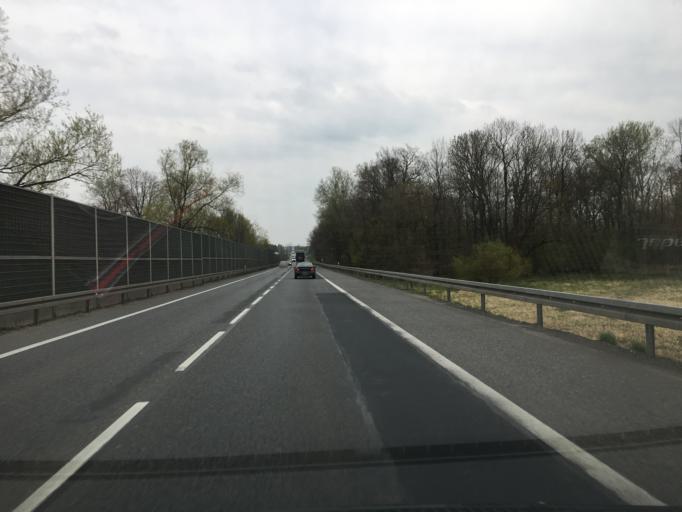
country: PL
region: Lower Silesian Voivodeship
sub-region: Powiat sredzki
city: Sroda Slaska
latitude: 51.1612
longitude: 16.5834
